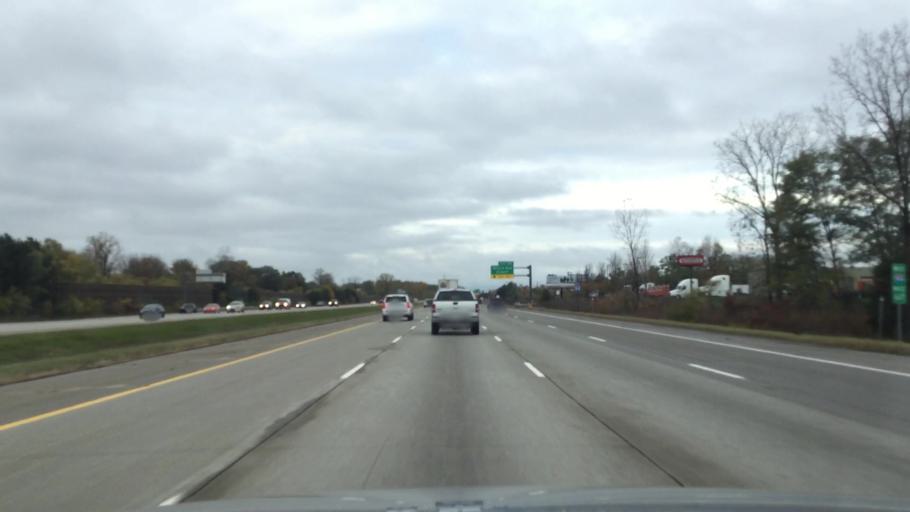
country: US
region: Michigan
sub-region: Wayne County
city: Belleville
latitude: 42.2184
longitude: -83.5473
